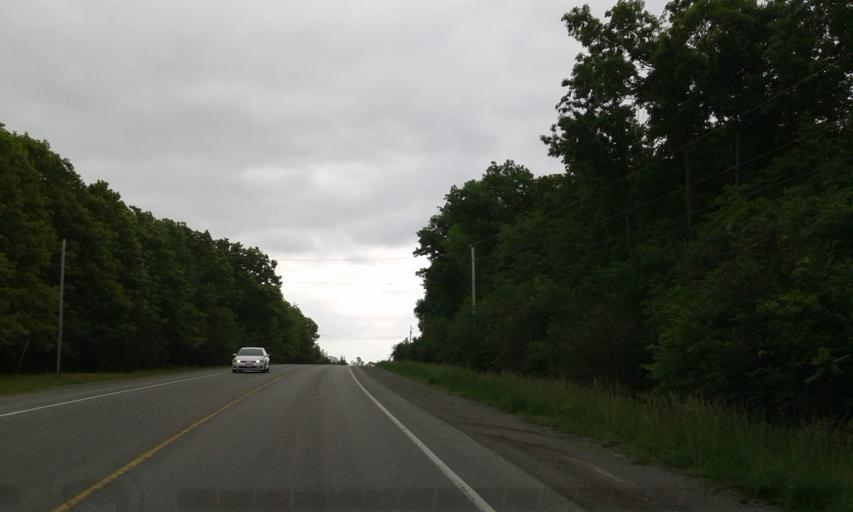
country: CA
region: Ontario
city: Quinte West
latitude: 43.9746
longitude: -77.5052
